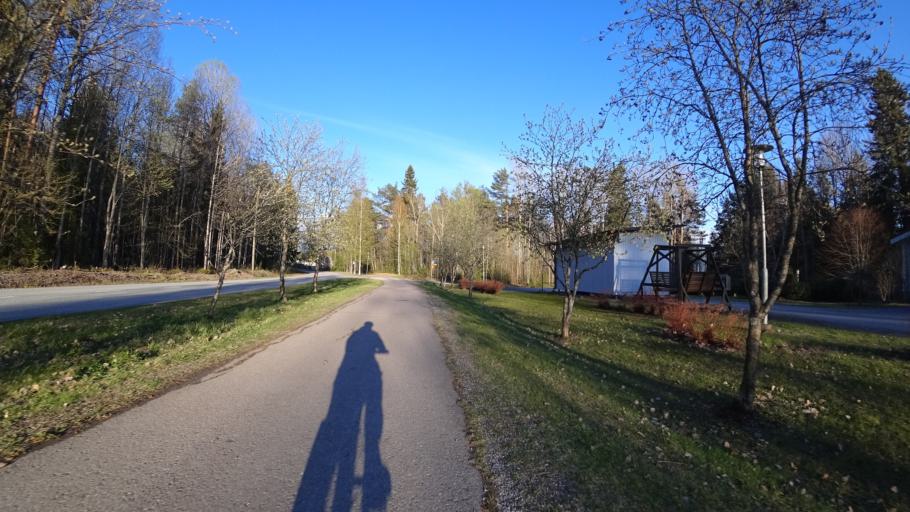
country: FI
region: Pirkanmaa
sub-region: Tampere
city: Nokia
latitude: 61.4911
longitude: 23.5485
